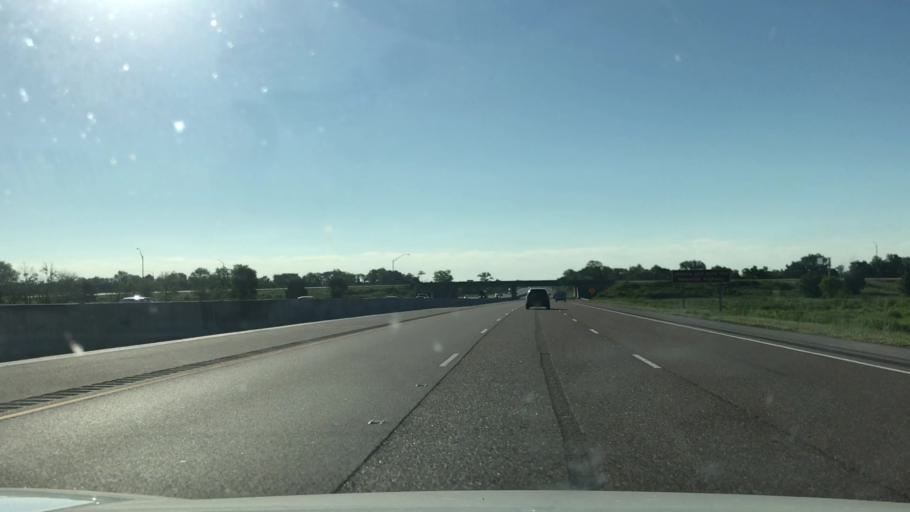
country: US
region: Illinois
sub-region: Saint Clair County
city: Shiloh
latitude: 38.5739
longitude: -89.8802
